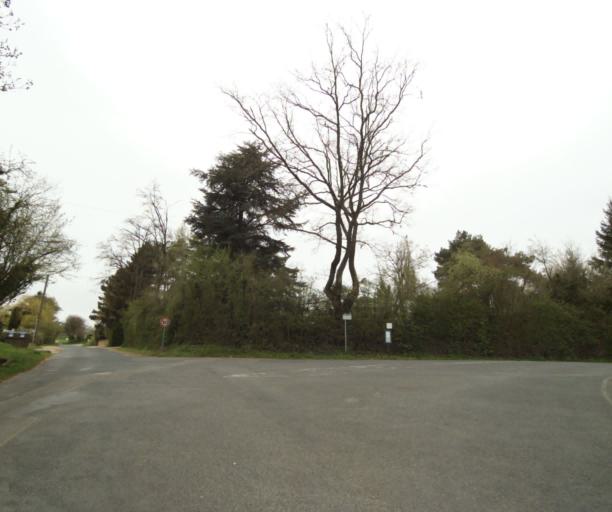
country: FR
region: Bourgogne
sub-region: Departement de Saone-et-Loire
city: Charnay-les-Macon
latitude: 46.3176
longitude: 4.8045
